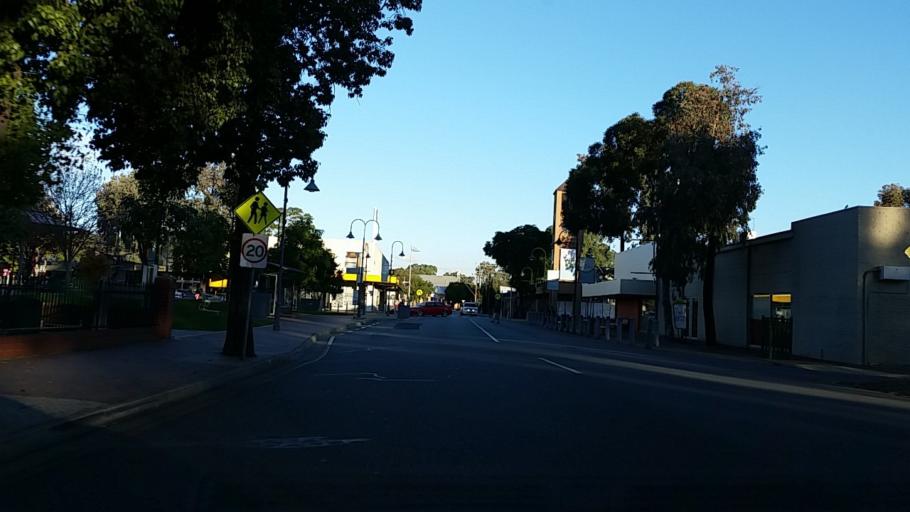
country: AU
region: South Australia
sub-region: Salisbury
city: Salisbury
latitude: -34.7617
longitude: 138.6450
